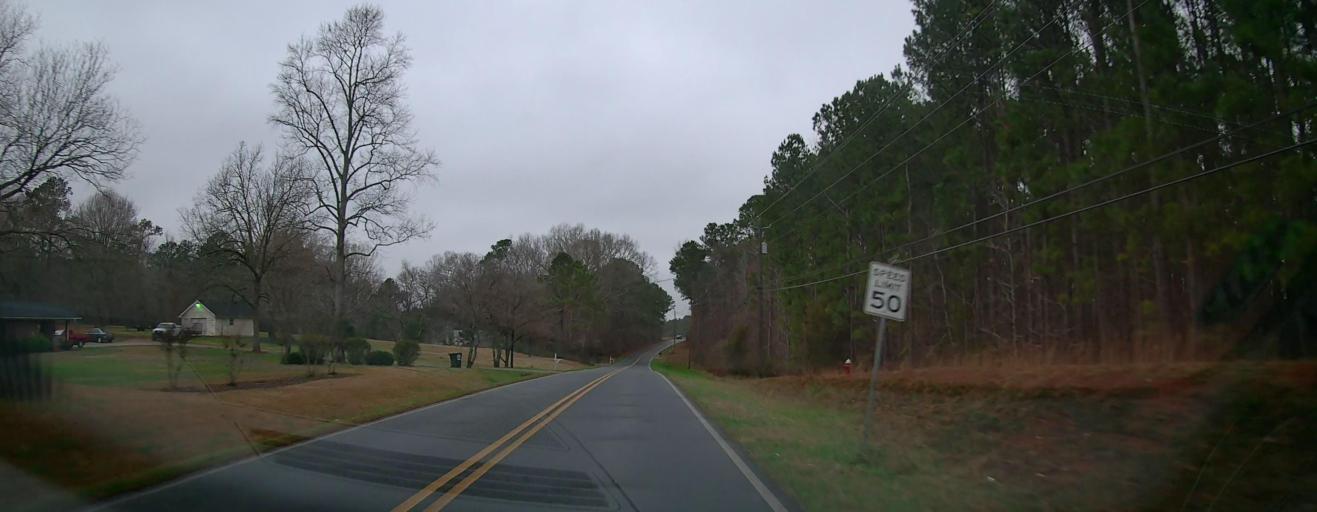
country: US
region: Georgia
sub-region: Pike County
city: Zebulon
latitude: 33.1177
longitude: -84.3440
